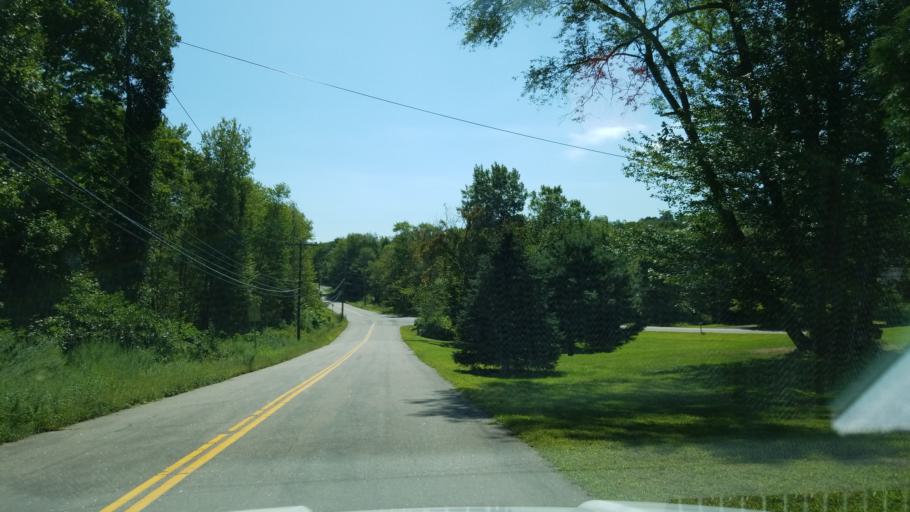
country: US
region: Connecticut
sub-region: Hartford County
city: Tariffville
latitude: 41.8523
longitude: -72.7535
